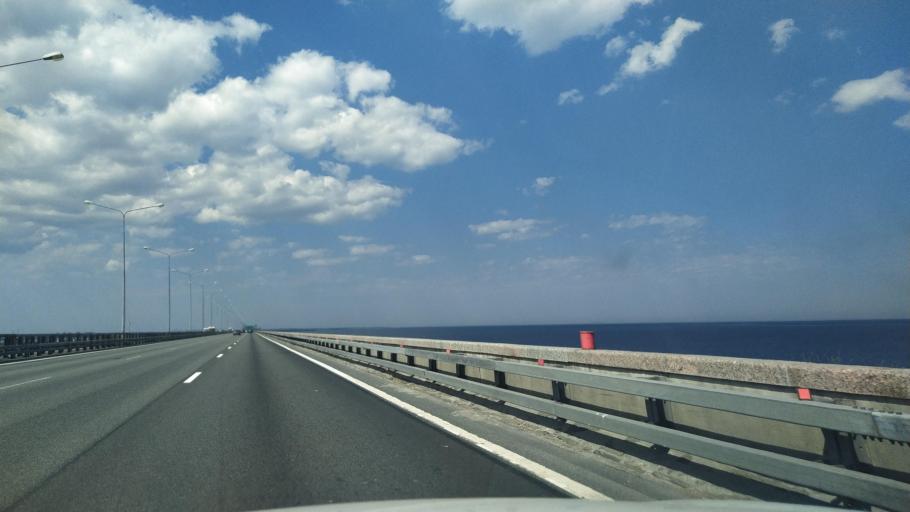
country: RU
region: Leningrad
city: Gorskaya
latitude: 60.0319
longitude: 29.8964
